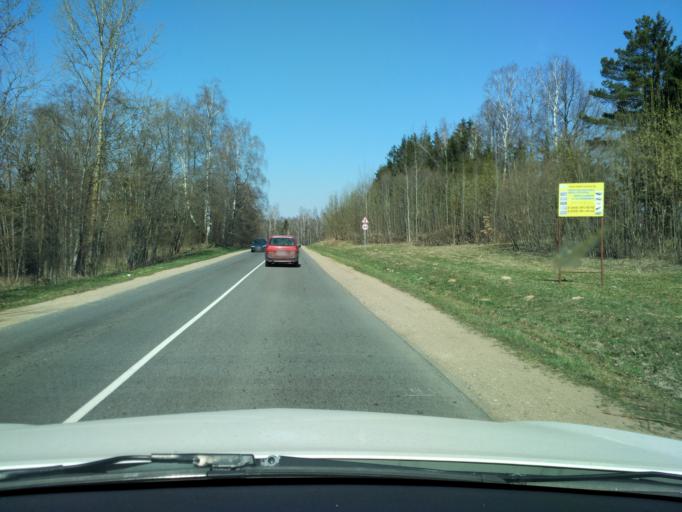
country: BY
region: Minsk
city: Slabada
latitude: 53.9869
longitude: 27.9574
